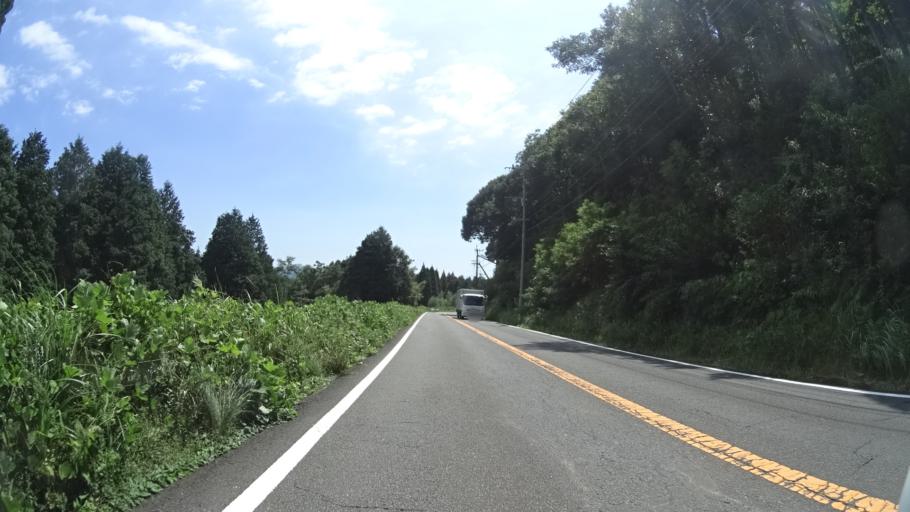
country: JP
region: Kagoshima
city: Kokubu-matsuki
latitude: 31.8690
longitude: 130.7885
